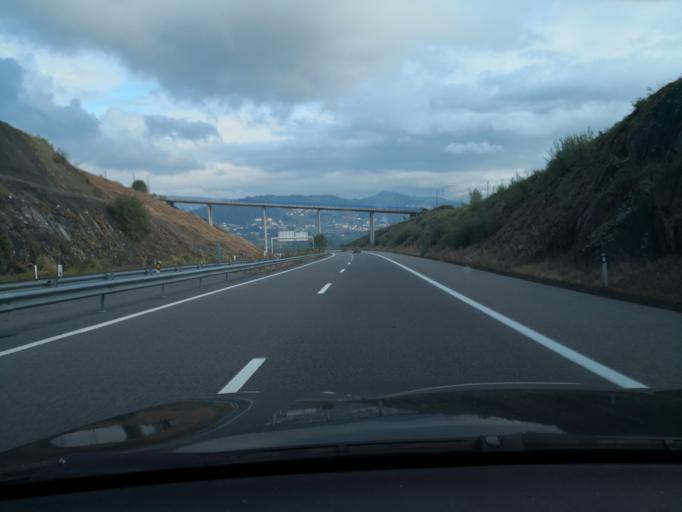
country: PT
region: Porto
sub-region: Felgueiras
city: Vizela
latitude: 41.3987
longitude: -8.2450
